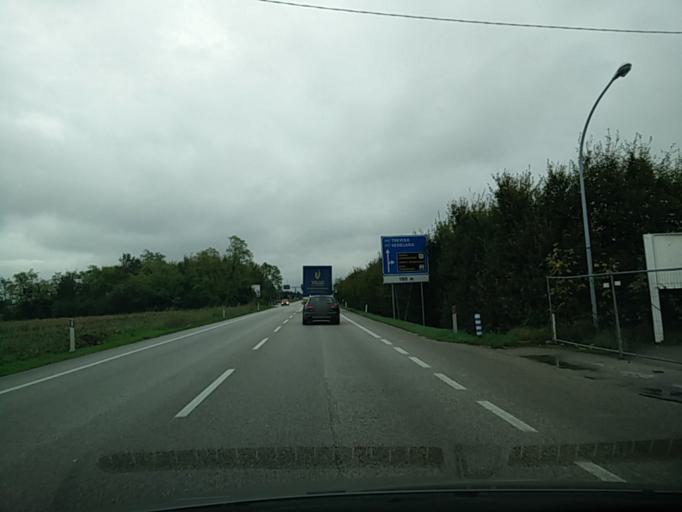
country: IT
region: Veneto
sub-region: Provincia di Treviso
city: Castelfranco Veneto
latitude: 45.6842
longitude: 11.9351
